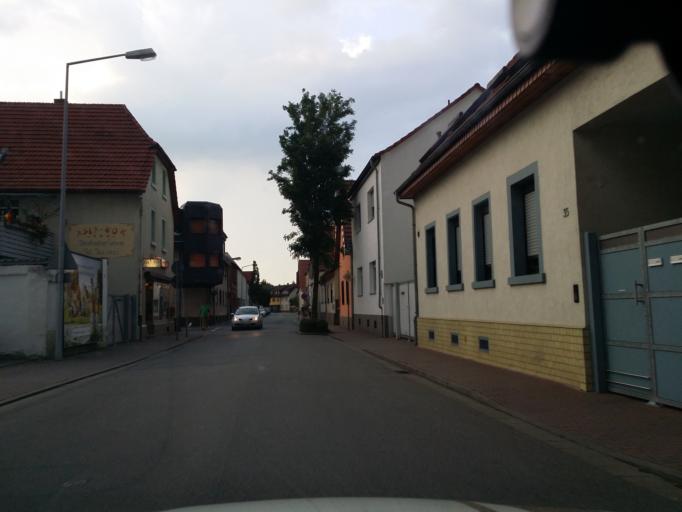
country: DE
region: Hesse
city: Viernheim
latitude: 49.5402
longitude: 8.5816
